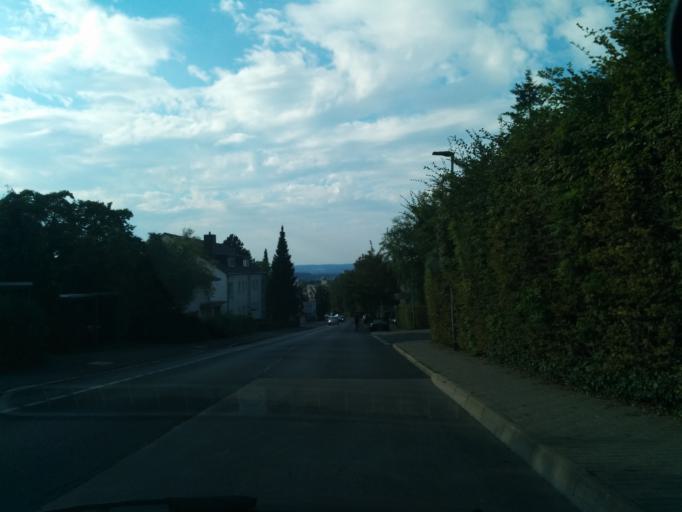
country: DE
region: Lower Saxony
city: Goettingen
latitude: 51.5251
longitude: 9.9578
